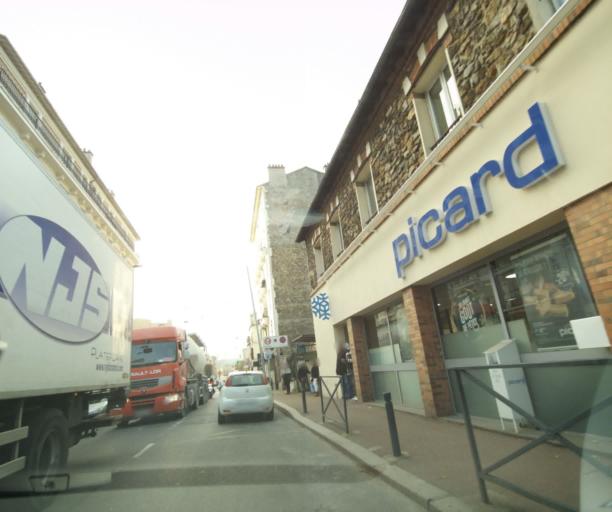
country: FR
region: Ile-de-France
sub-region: Departement de Seine-Saint-Denis
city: Gagny
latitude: 48.8827
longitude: 2.5257
